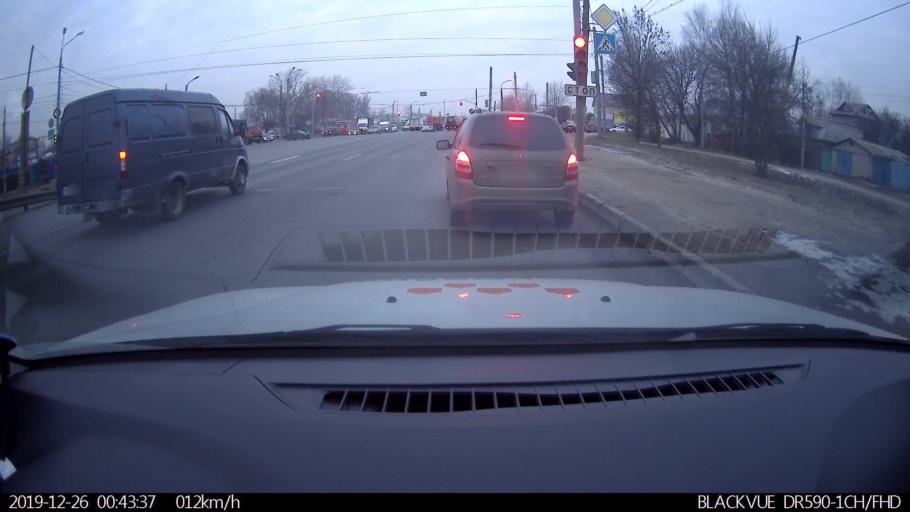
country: RU
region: Nizjnij Novgorod
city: Nizhniy Novgorod
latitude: 56.3002
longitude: 43.8755
